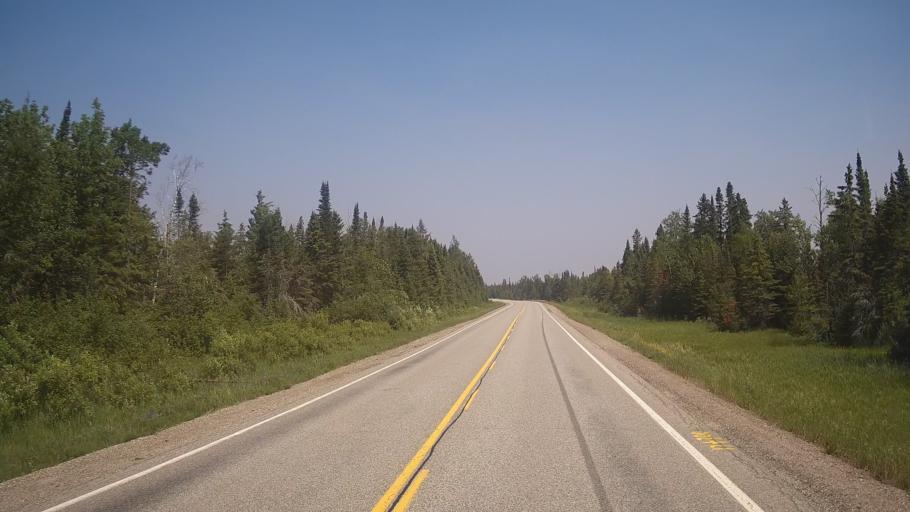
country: CA
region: Ontario
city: Timmins
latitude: 48.1680
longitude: -81.5834
